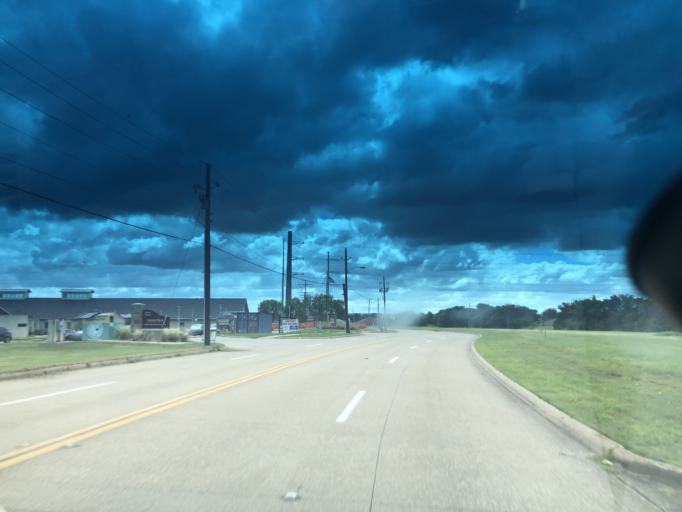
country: US
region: Texas
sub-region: Dallas County
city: Grand Prairie
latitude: 32.6984
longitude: -97.0368
